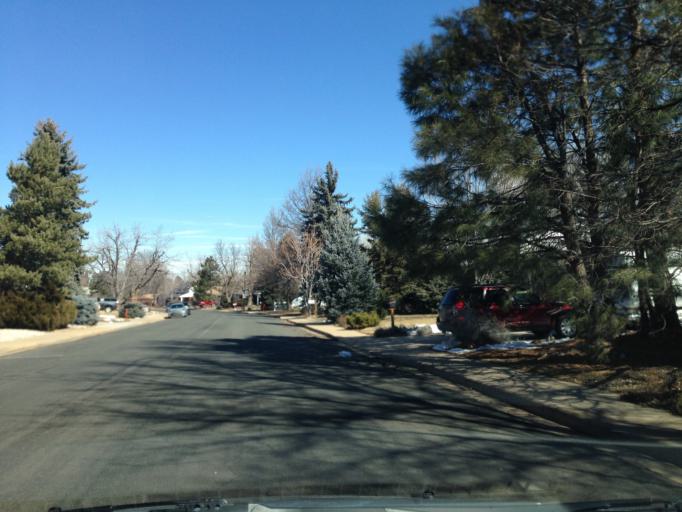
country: US
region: Colorado
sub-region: Boulder County
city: Boulder
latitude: 39.9882
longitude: -105.2275
